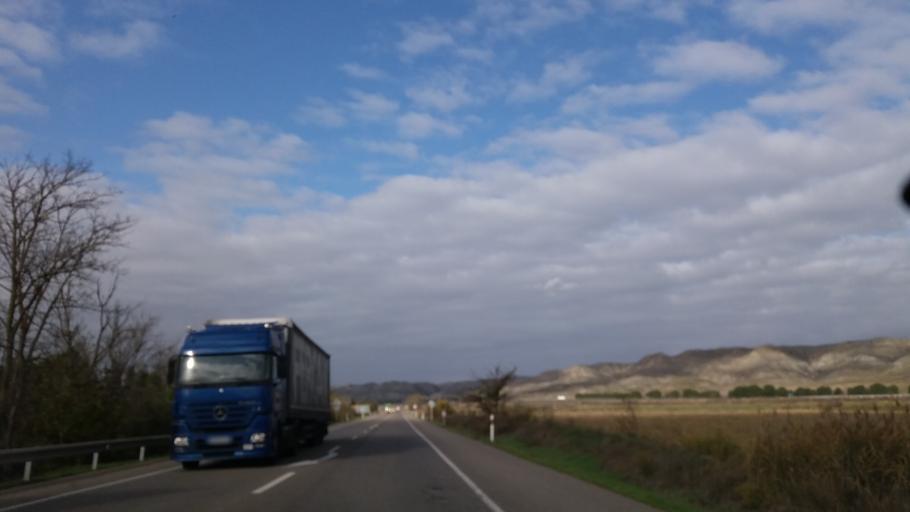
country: ES
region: Aragon
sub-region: Provincia de Zaragoza
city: Fuentes de Ebro
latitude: 41.5379
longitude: -0.5809
